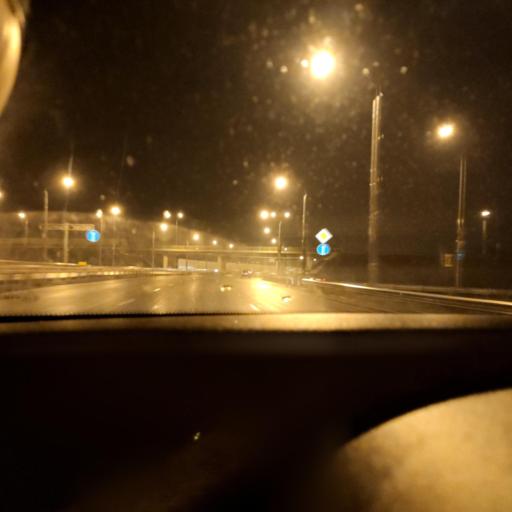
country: RU
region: Samara
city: Samara
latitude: 53.1639
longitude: 50.0866
